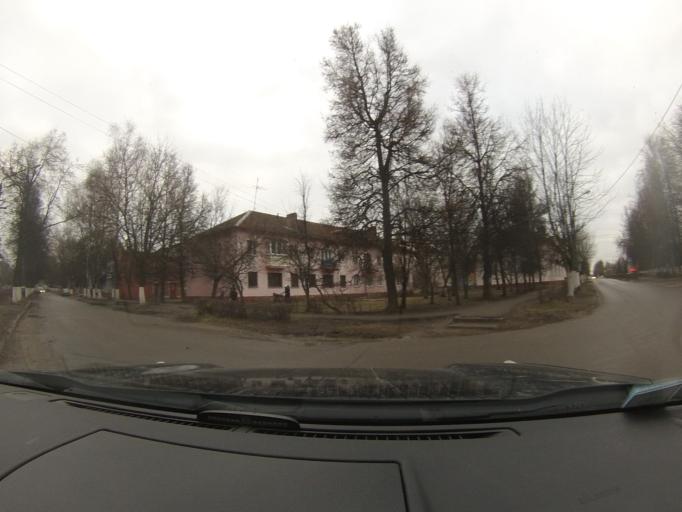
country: RU
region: Moskovskaya
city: Lopatinskiy
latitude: 55.3427
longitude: 38.7213
